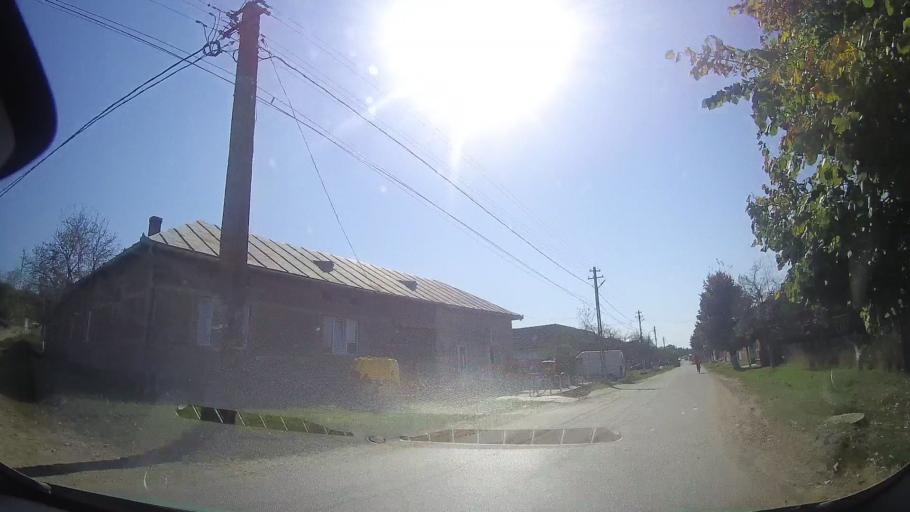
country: RO
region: Timis
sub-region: Comuna Bethausen
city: Bethausen
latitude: 45.8638
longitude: 21.9705
